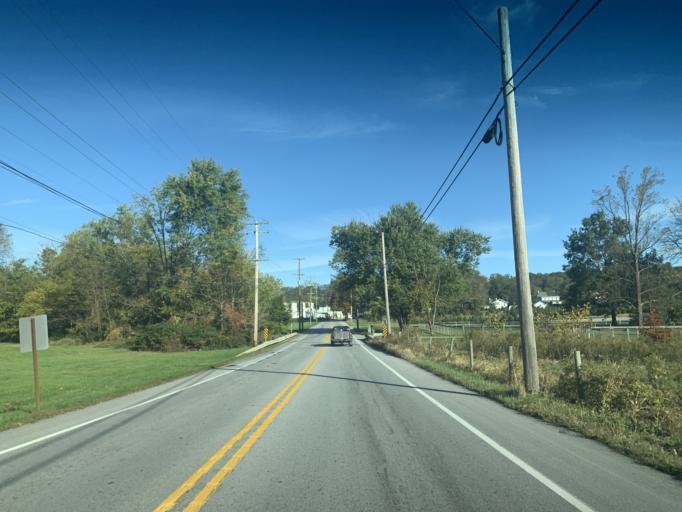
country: US
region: Pennsylvania
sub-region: Chester County
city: Parkesburg
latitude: 39.9558
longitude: -75.9118
